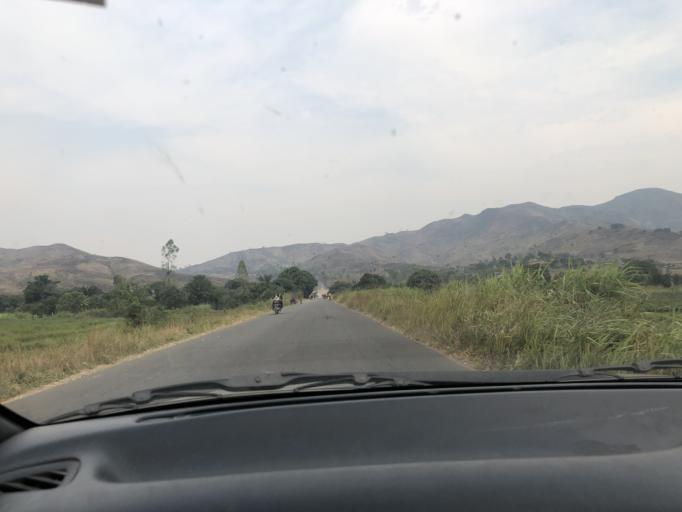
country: BI
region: Cibitoke
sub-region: Commune of Buganda
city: Buganda
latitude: -3.0892
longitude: 29.1274
